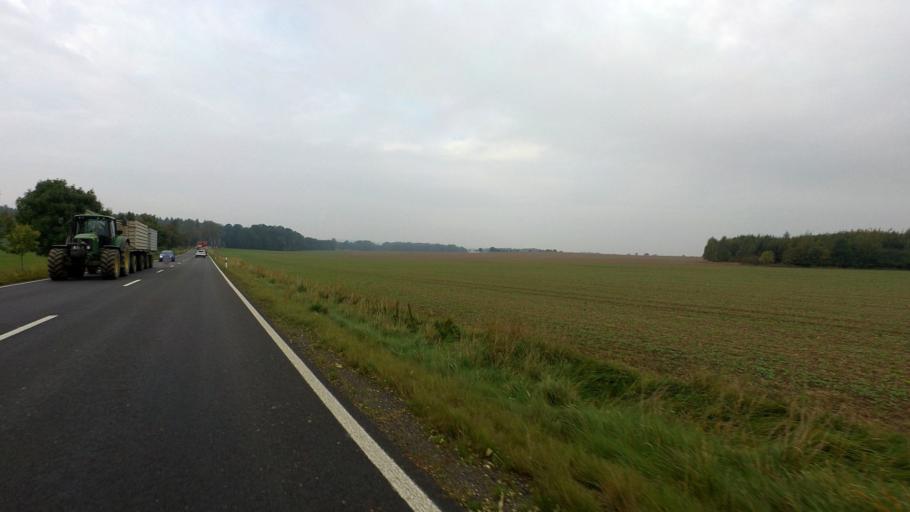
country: DE
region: Saxony
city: Stolpen
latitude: 51.0874
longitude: 14.0573
